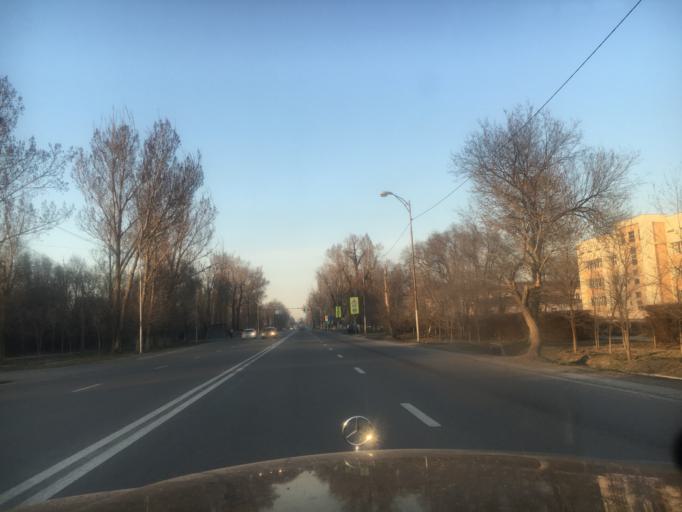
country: KZ
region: Almaty Oblysy
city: Pervomayskiy
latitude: 43.3724
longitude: 76.9902
